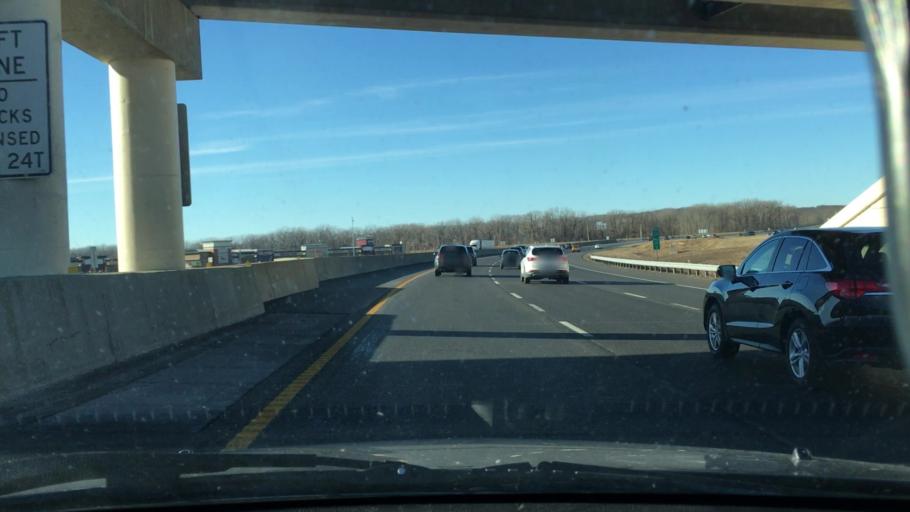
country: US
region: Missouri
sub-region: Saint Charles County
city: Weldon Spring
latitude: 38.6767
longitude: -90.6563
